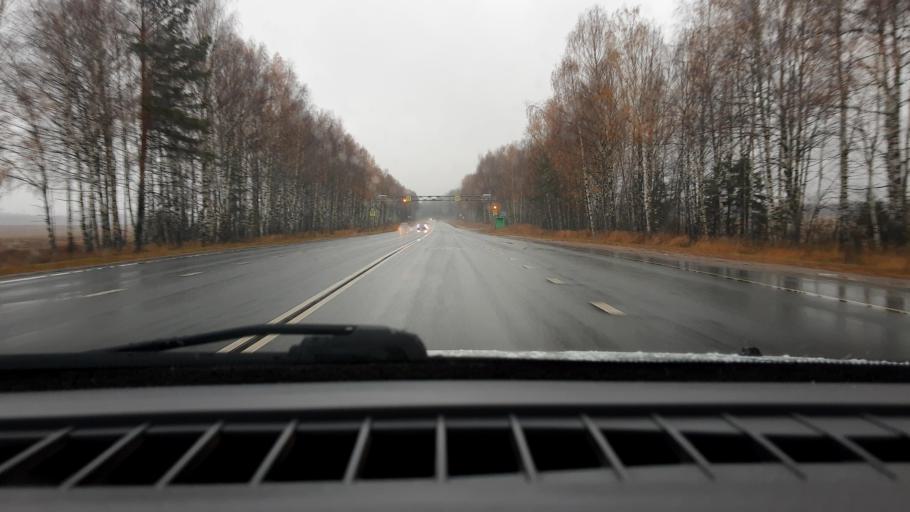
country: RU
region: Nizjnij Novgorod
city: Linda
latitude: 56.6550
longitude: 44.1208
